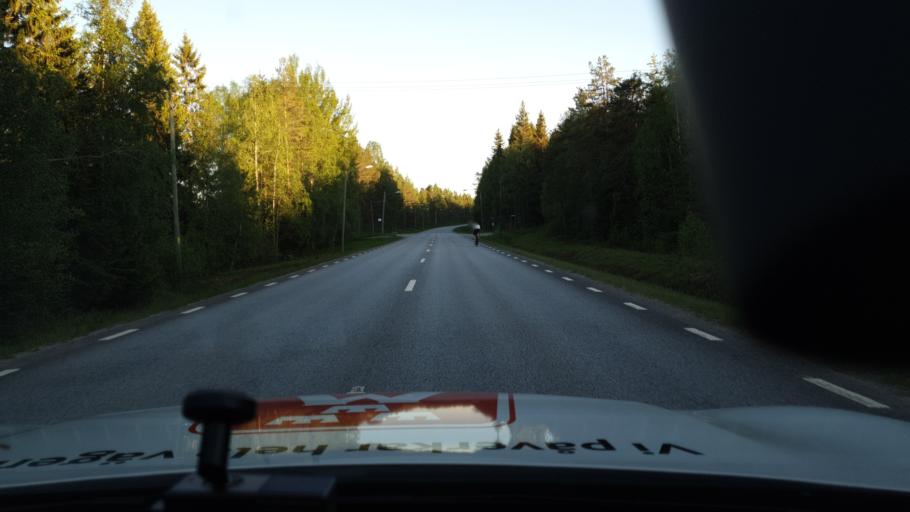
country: SE
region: Vaesterbotten
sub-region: Umea Kommun
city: Ersmark
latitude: 63.8819
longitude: 20.3068
